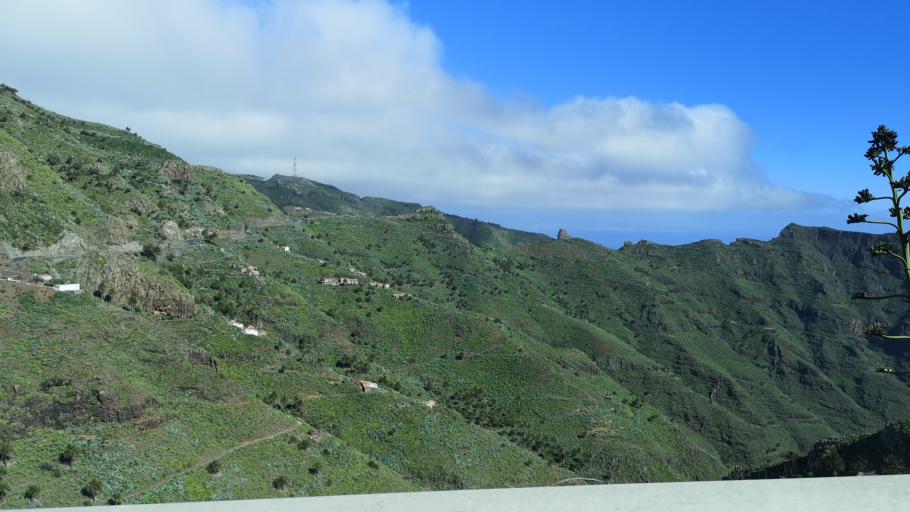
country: ES
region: Canary Islands
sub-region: Provincia de Santa Cruz de Tenerife
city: Alajero
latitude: 28.0899
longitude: -17.2003
